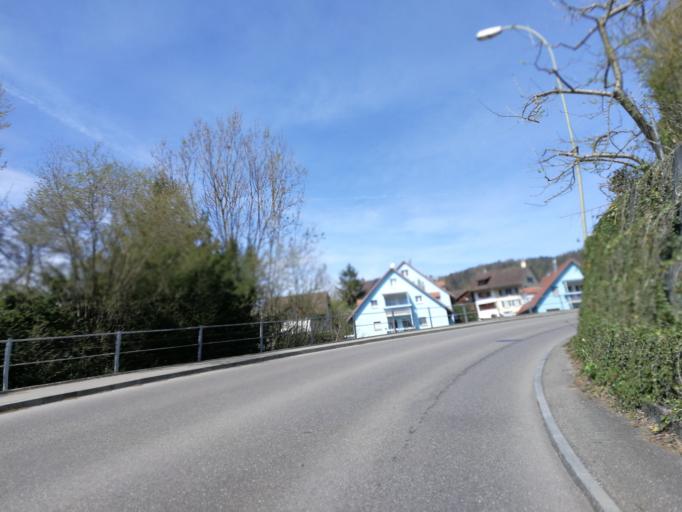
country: CH
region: Zurich
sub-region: Bezirk Meilen
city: Mannedorf
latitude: 47.2562
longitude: 8.7023
